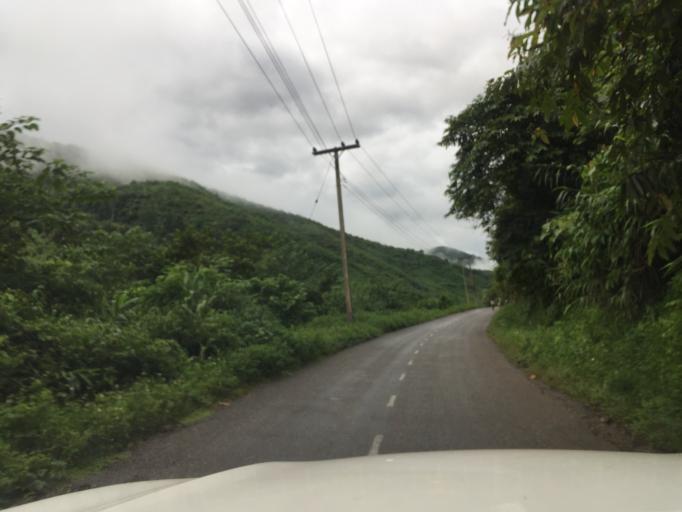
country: LA
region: Oudomxai
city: Muang La
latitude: 21.0425
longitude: 102.2416
